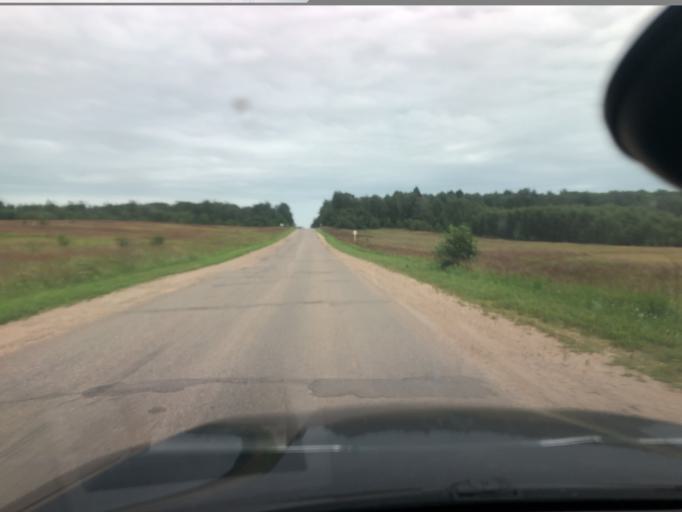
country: RU
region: Jaroslavl
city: Petrovsk
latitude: 56.9846
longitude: 39.1476
